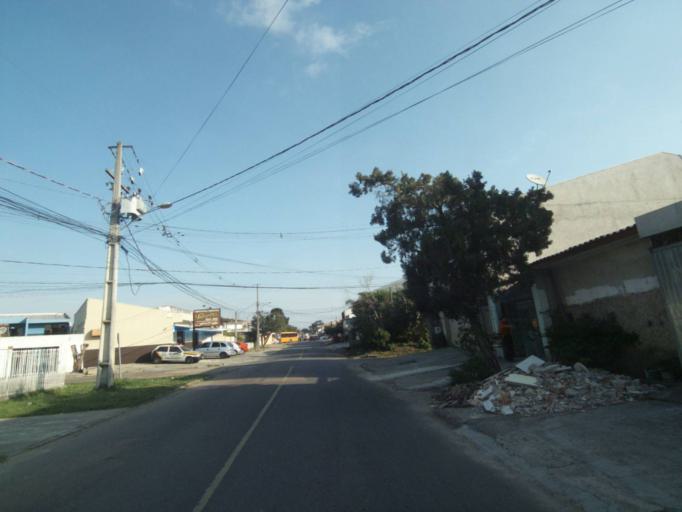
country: BR
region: Parana
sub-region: Curitiba
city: Curitiba
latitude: -25.4858
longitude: -49.3364
